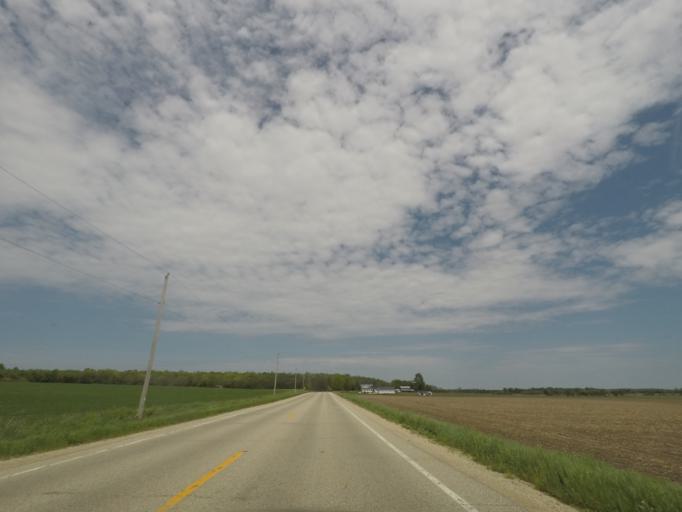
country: US
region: Wisconsin
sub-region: Rock County
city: Evansville
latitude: 42.7206
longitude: -89.2888
